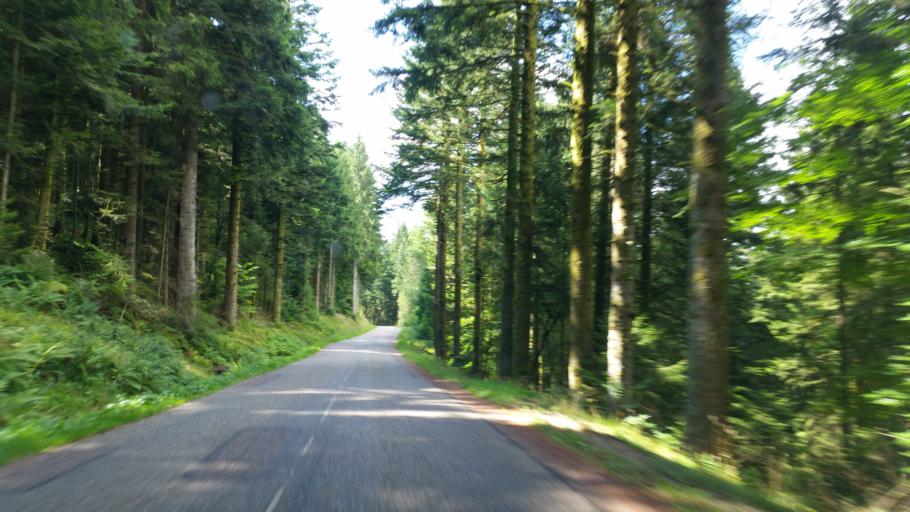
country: FR
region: Lorraine
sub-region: Departement des Vosges
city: Le Tholy
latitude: 48.0868
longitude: 6.7972
